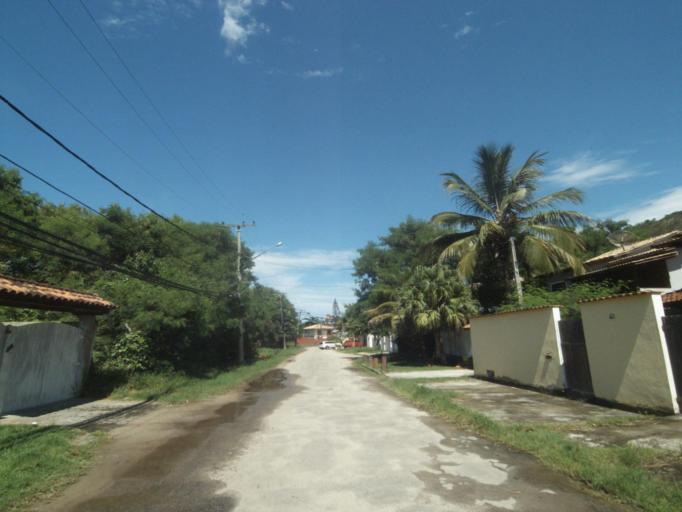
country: BR
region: Rio de Janeiro
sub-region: Niteroi
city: Niteroi
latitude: -22.9461
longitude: -43.0411
